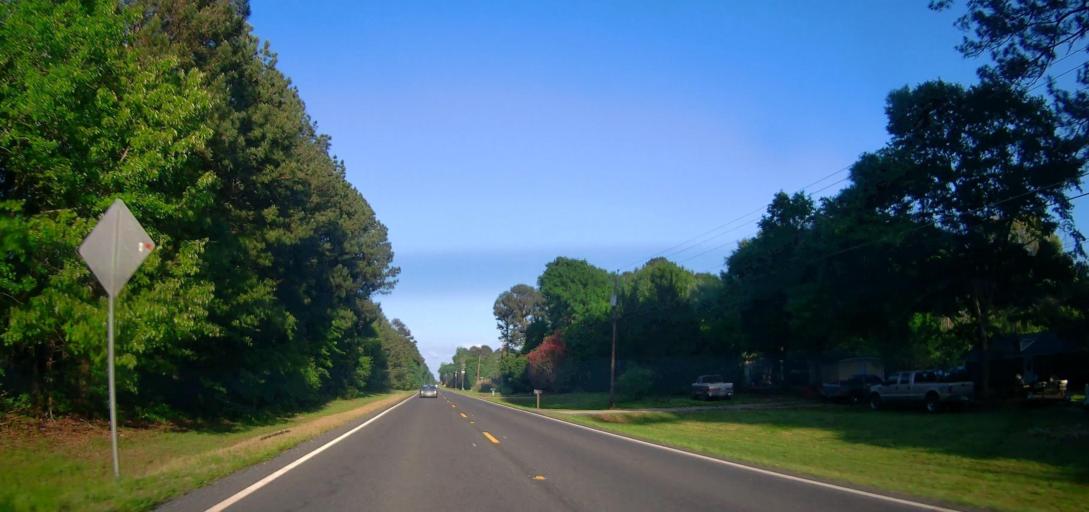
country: US
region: Georgia
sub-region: Walton County
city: Social Circle
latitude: 33.5095
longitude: -83.6777
